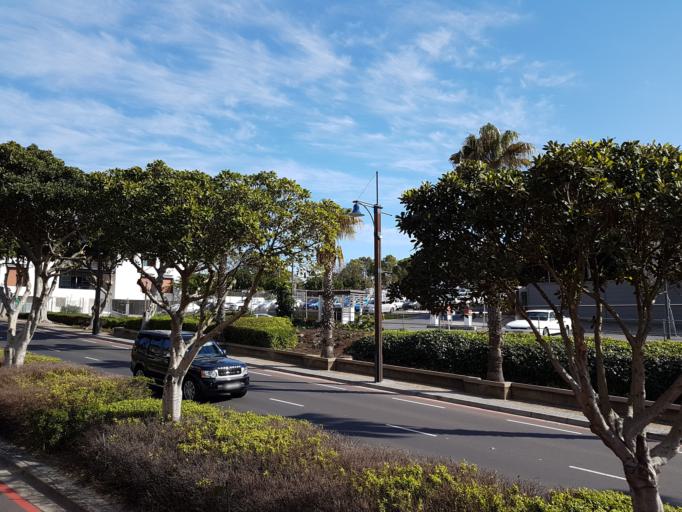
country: ZA
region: Western Cape
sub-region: City of Cape Town
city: Cape Town
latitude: -33.9085
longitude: 18.4159
